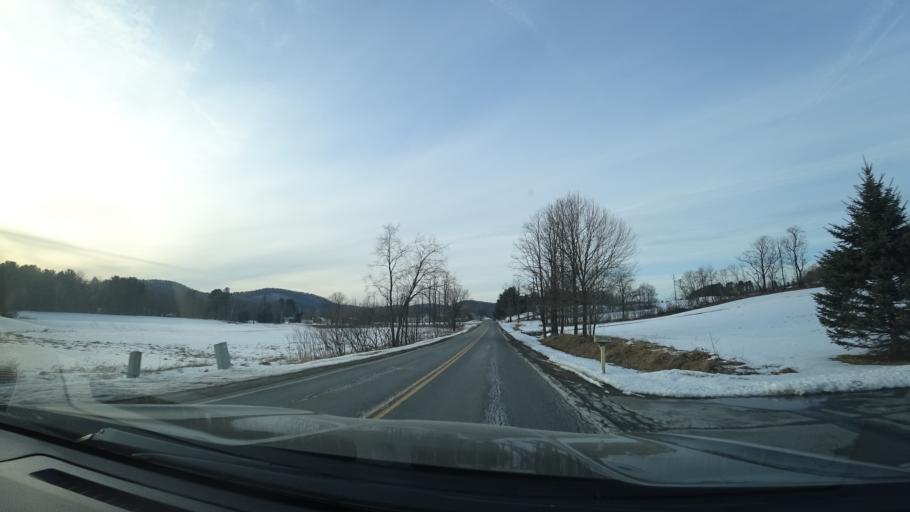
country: US
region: New York
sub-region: Washington County
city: Cambridge
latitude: 43.1687
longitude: -73.3504
